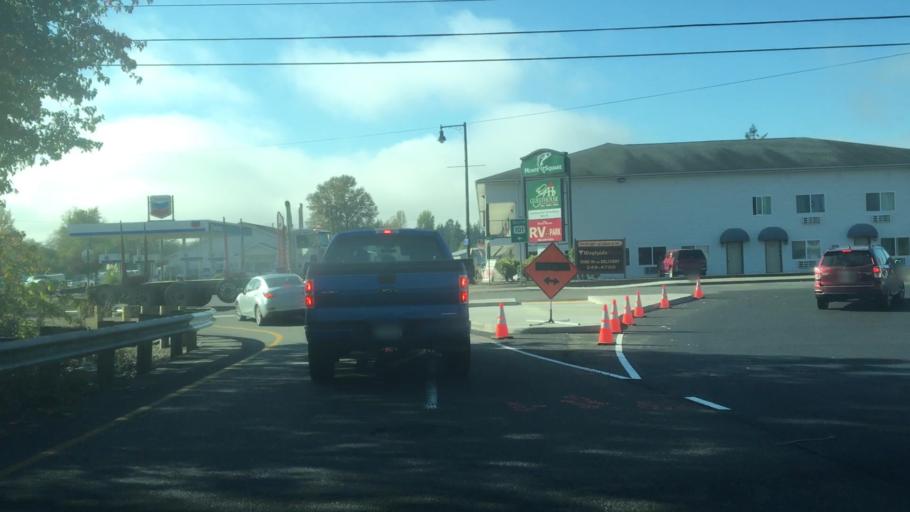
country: US
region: Washington
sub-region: Grays Harbor County
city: Montesano
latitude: 46.9770
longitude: -123.6005
